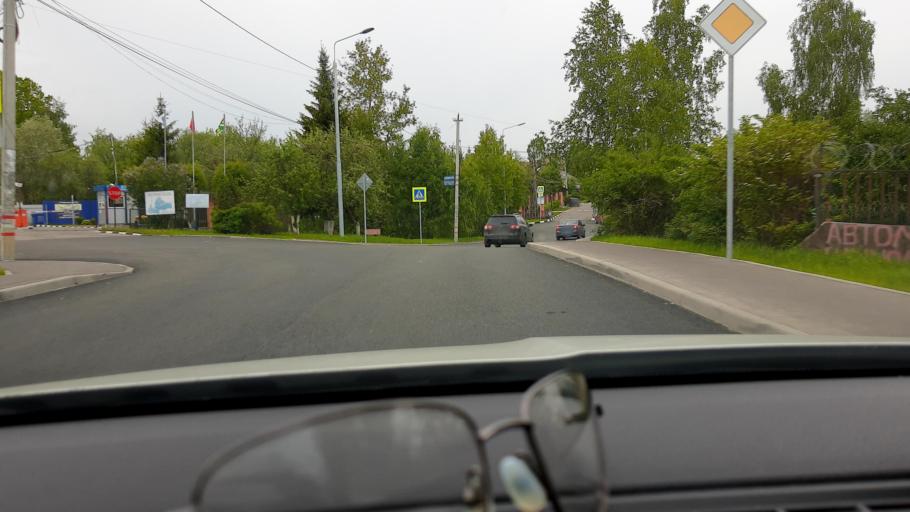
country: RU
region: Moskovskaya
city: Vatutinki
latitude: 55.5177
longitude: 37.3266
